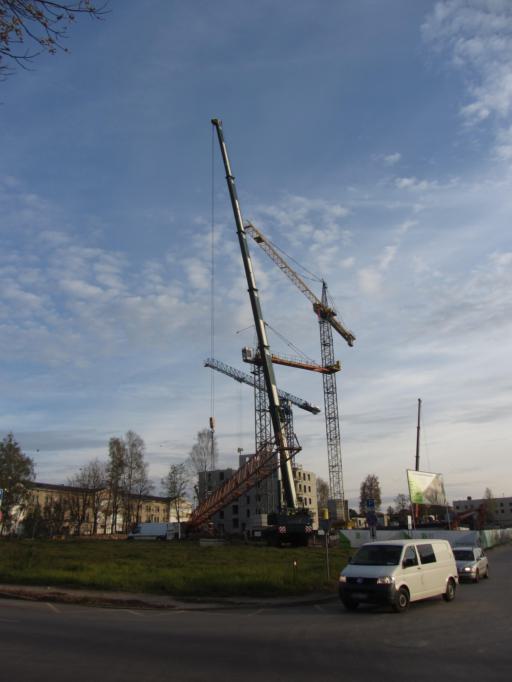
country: LT
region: Vilnius County
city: Naujamiestis
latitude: 54.6764
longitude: 25.2581
